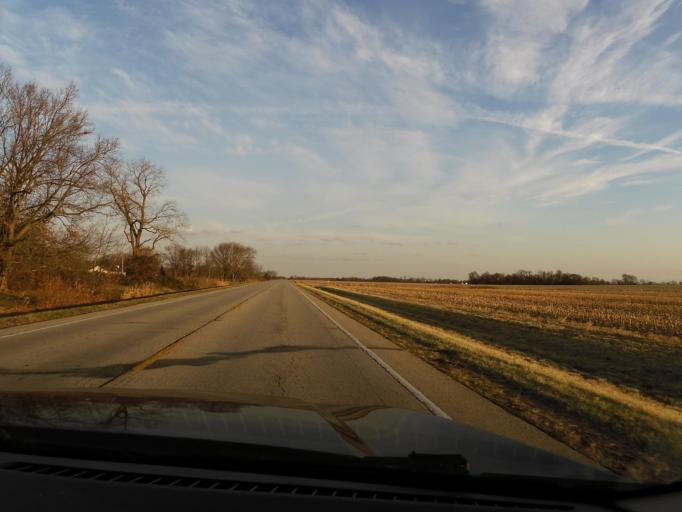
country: US
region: Illinois
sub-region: Fayette County
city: Vandalia
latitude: 38.8692
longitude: -89.0857
